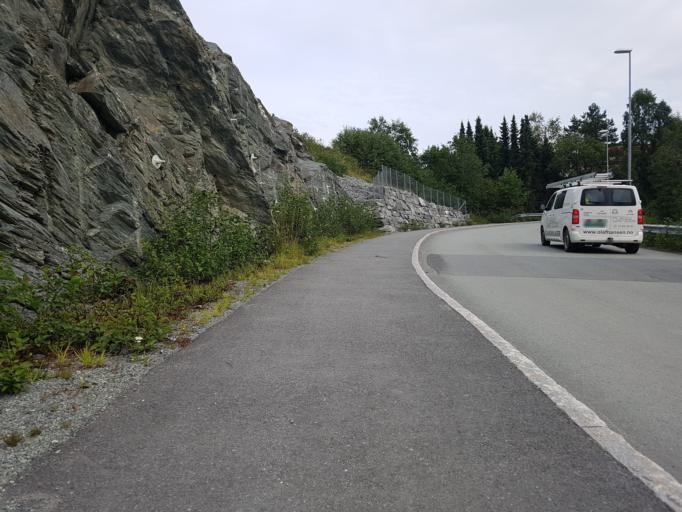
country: NO
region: Sor-Trondelag
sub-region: Trondheim
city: Trondheim
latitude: 63.3844
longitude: 10.3653
